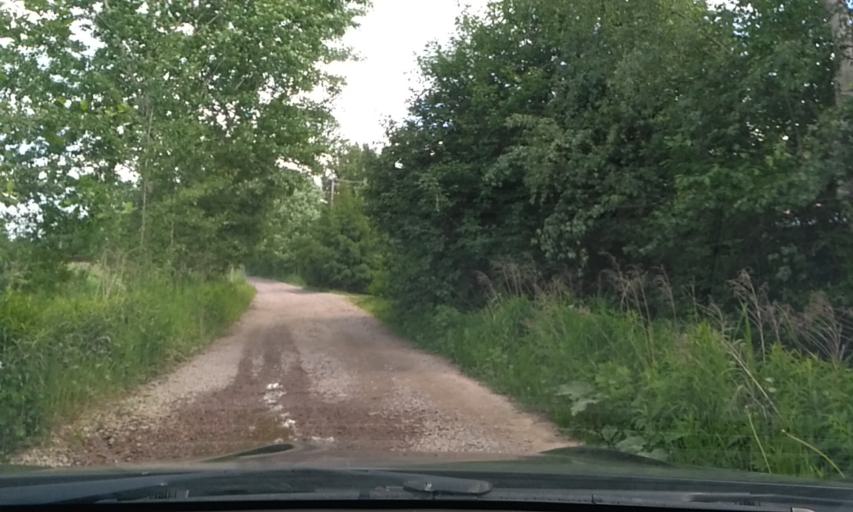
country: RU
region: Leningrad
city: Otradnoye
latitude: 59.8062
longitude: 30.8266
